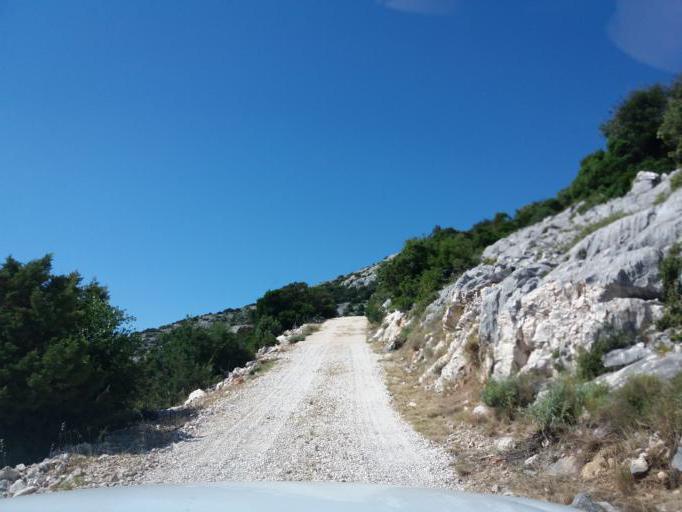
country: HR
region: Zadarska
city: Ugljan
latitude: 44.0058
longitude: 15.0363
